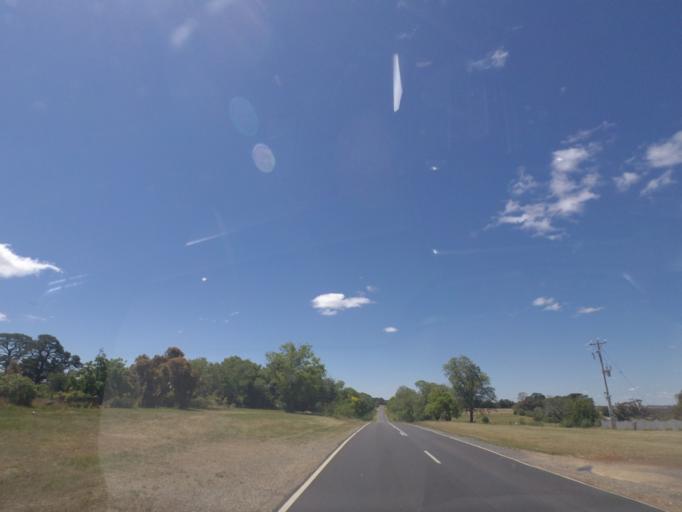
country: AU
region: Victoria
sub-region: Mount Alexander
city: Castlemaine
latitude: -37.2404
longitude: 144.3264
